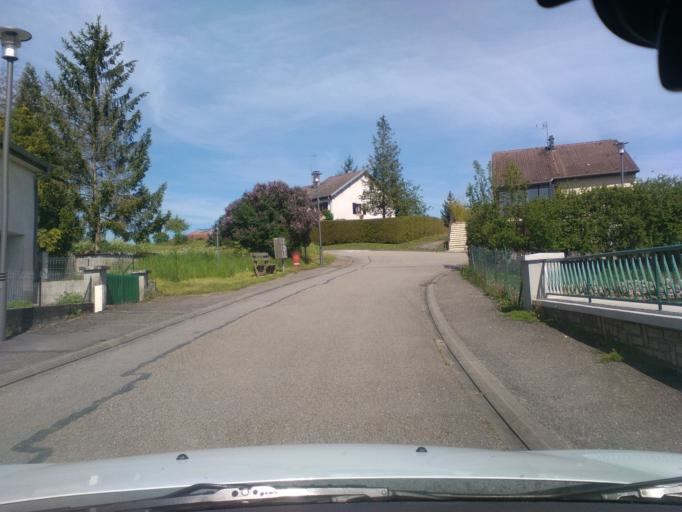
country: FR
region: Lorraine
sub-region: Departement des Vosges
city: Mirecourt
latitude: 48.3226
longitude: 6.1228
